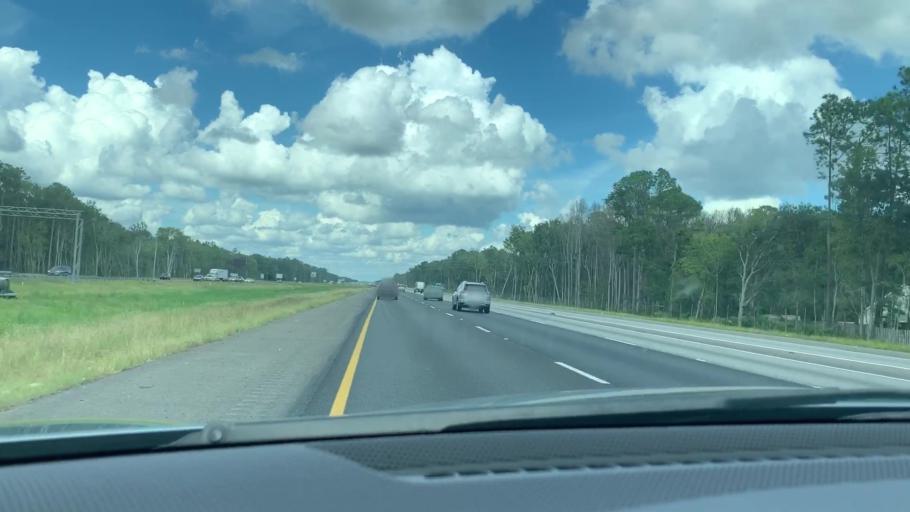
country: US
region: Georgia
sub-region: Camden County
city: Kingsland
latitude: 30.7961
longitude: -81.6598
